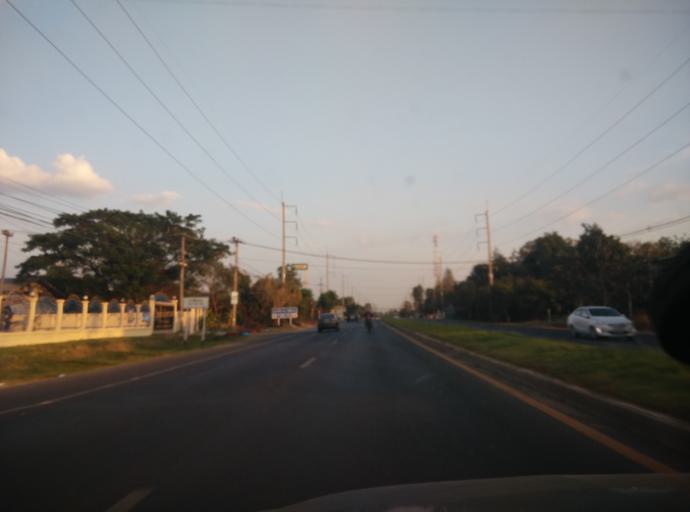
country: TH
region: Sisaket
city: Si Sa Ket
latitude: 15.1313
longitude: 104.2749
